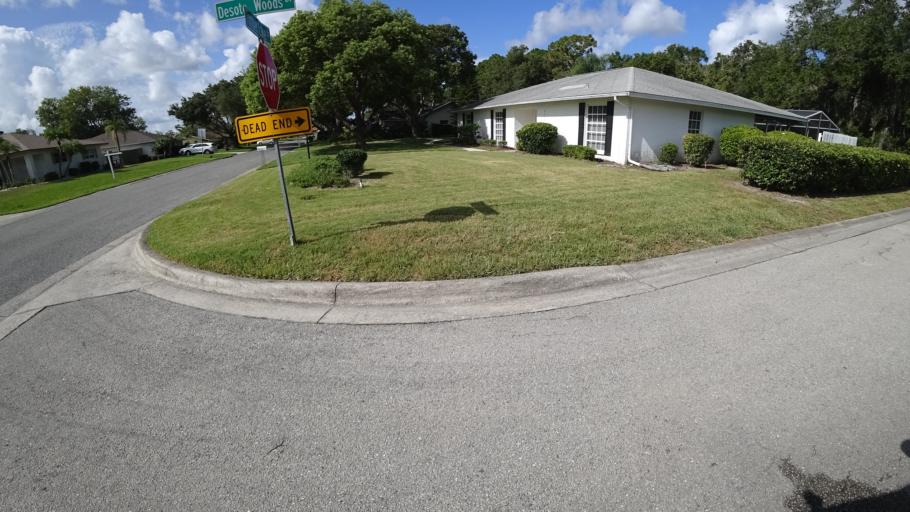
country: US
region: Florida
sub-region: Sarasota County
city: Desoto Lakes
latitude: 27.3962
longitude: -82.4887
